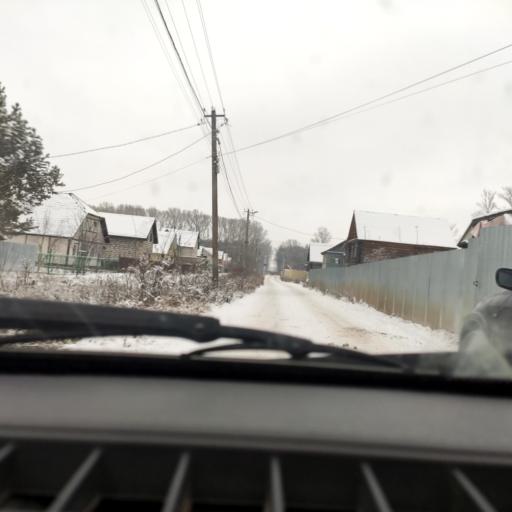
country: RU
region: Bashkortostan
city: Ufa
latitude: 54.6327
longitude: 55.8898
